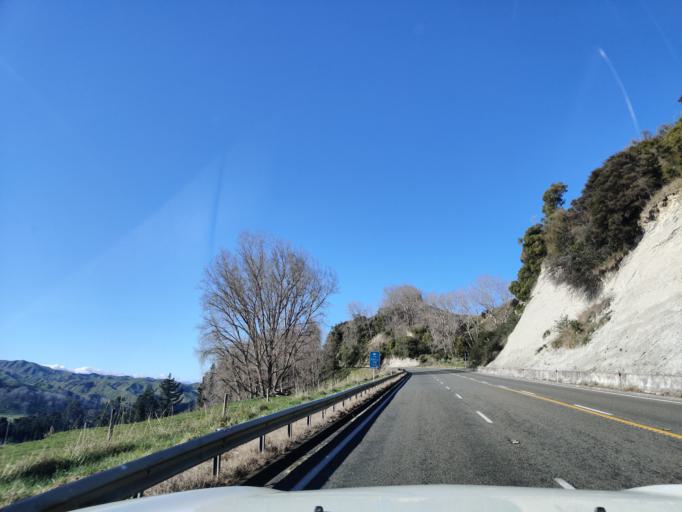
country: NZ
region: Manawatu-Wanganui
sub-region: Ruapehu District
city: Waiouru
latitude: -39.8246
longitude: 175.7770
